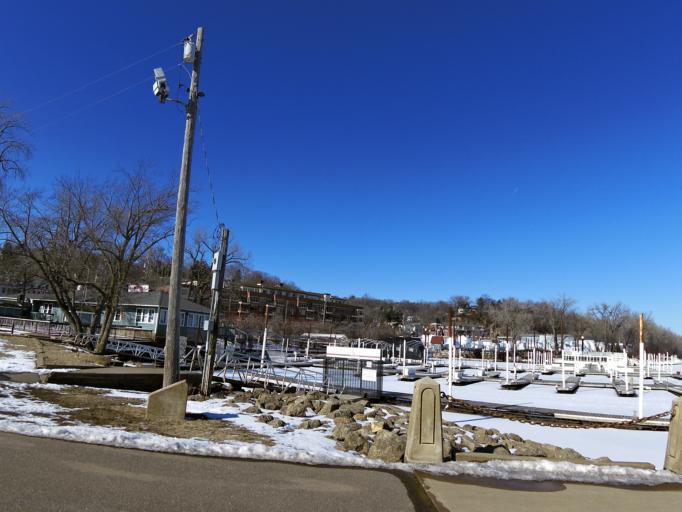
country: US
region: Minnesota
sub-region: Washington County
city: Stillwater
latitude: 45.0591
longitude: -92.8046
